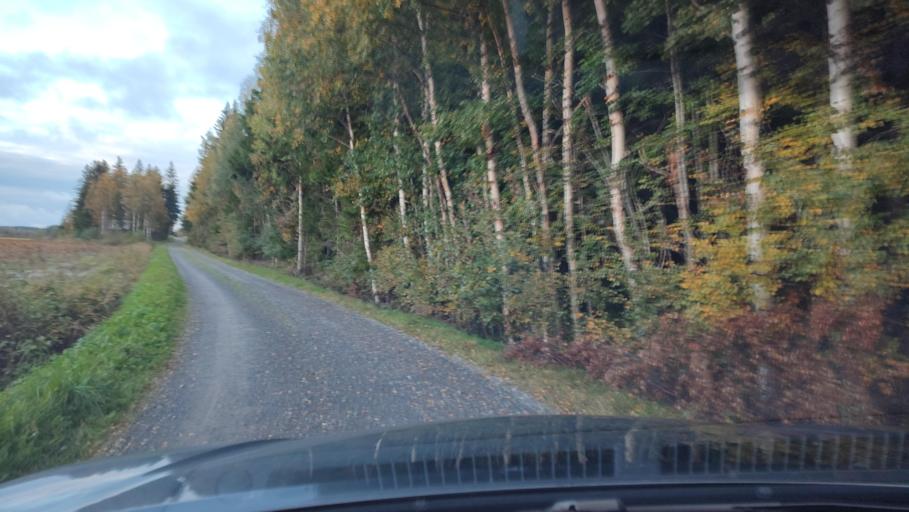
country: FI
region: Ostrobothnia
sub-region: Sydosterbotten
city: Kristinestad
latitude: 62.2452
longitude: 21.4525
